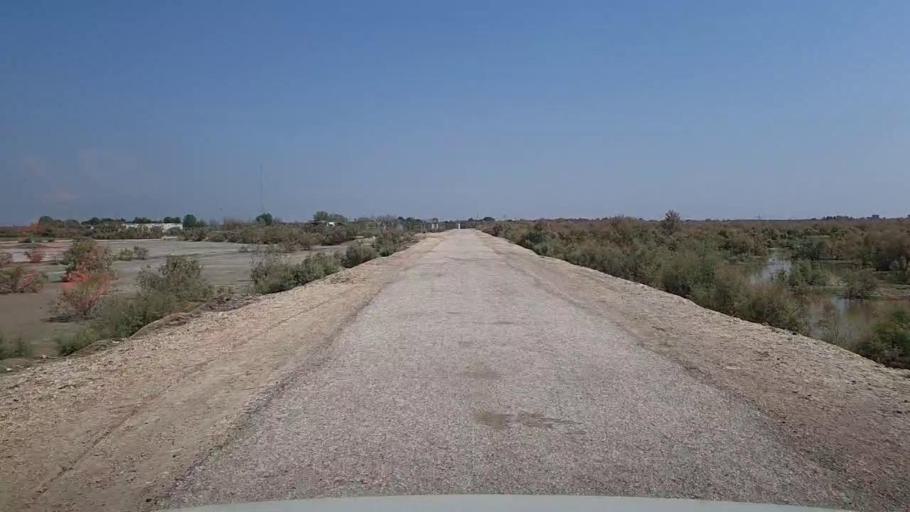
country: PK
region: Sindh
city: Kandhkot
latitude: 28.3029
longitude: 69.3480
